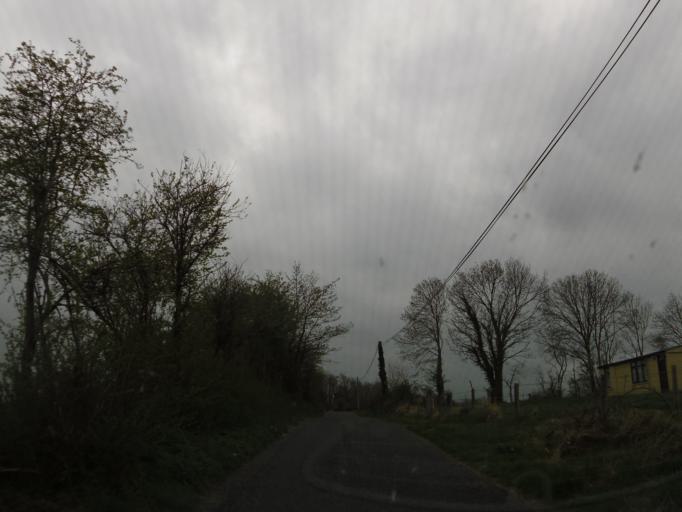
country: IE
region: Connaught
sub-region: Maigh Eo
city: Kiltamagh
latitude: 53.7954
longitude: -8.9657
